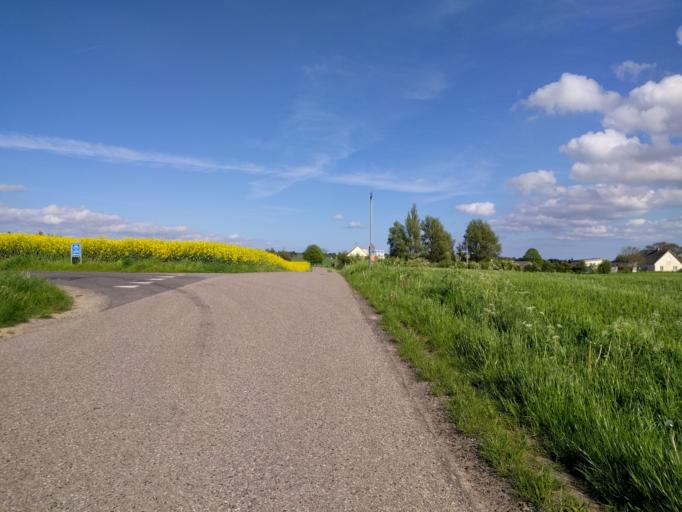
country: DK
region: Zealand
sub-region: Guldborgsund Kommune
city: Stubbekobing
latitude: 54.9260
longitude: 12.0274
